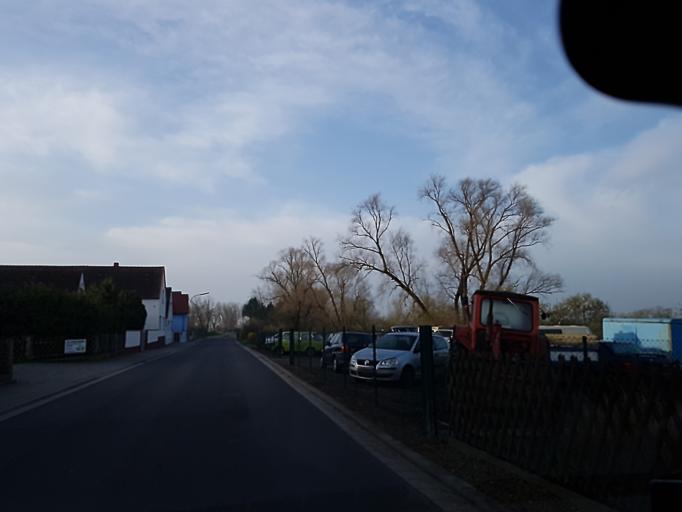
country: DE
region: Brandenburg
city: Muhlberg
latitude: 51.4173
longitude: 13.2674
